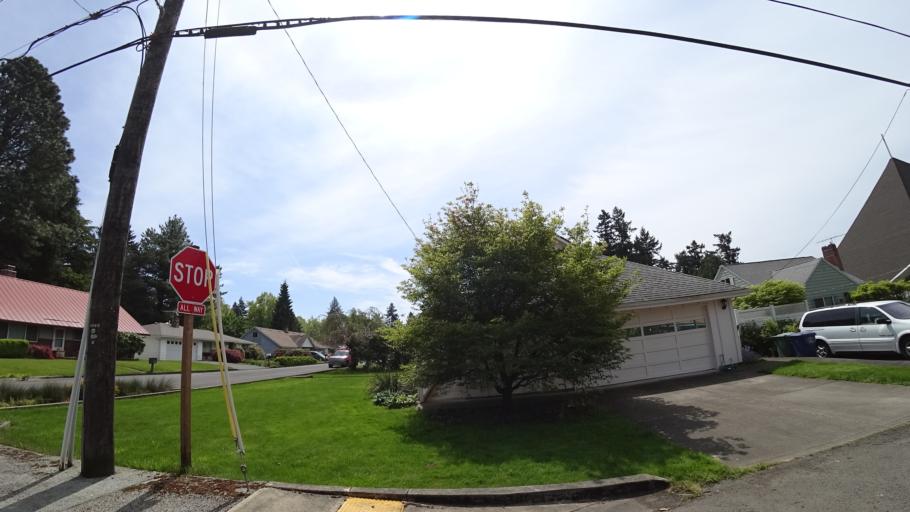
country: US
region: Oregon
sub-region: Clackamas County
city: Milwaukie
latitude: 45.4505
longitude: -122.6128
